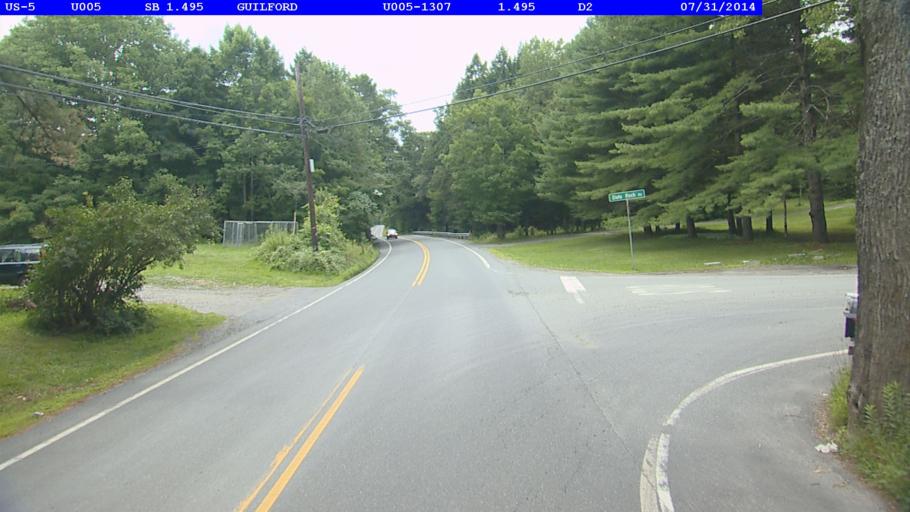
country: US
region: Massachusetts
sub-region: Franklin County
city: Bernardston
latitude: 42.7511
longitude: -72.5695
